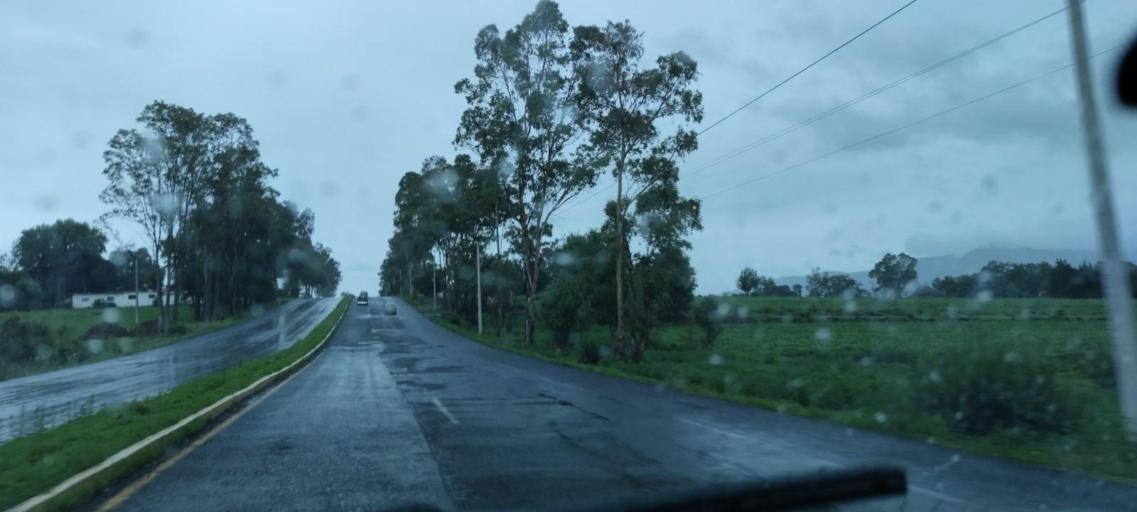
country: MX
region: Mexico
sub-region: Jilotepec
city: Doxhicho
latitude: 19.9143
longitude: -99.6026
